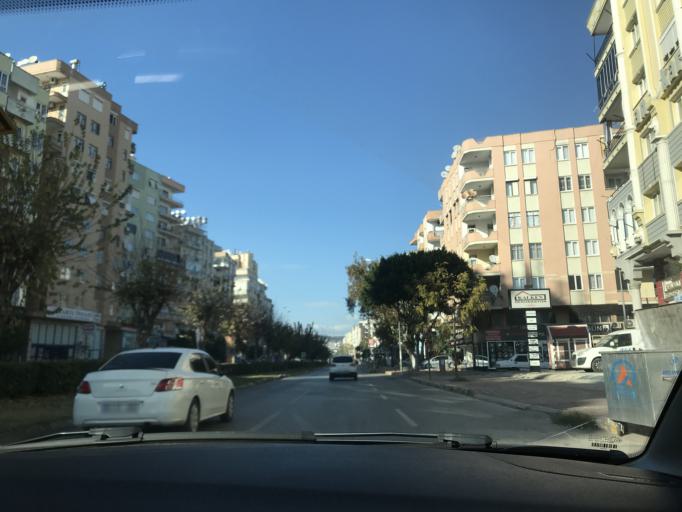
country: TR
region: Antalya
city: Antalya
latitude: 36.9046
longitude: 30.7007
